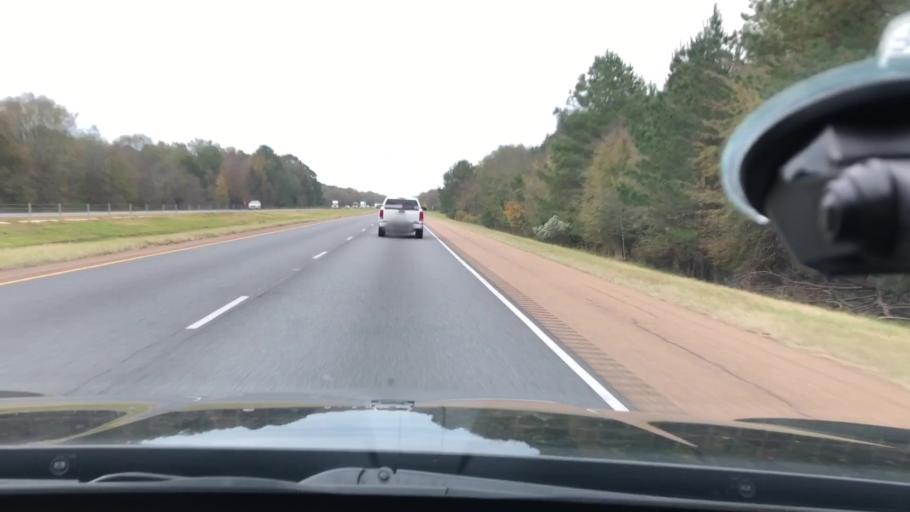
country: US
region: Arkansas
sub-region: Nevada County
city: Prescott
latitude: 33.8870
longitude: -93.3191
